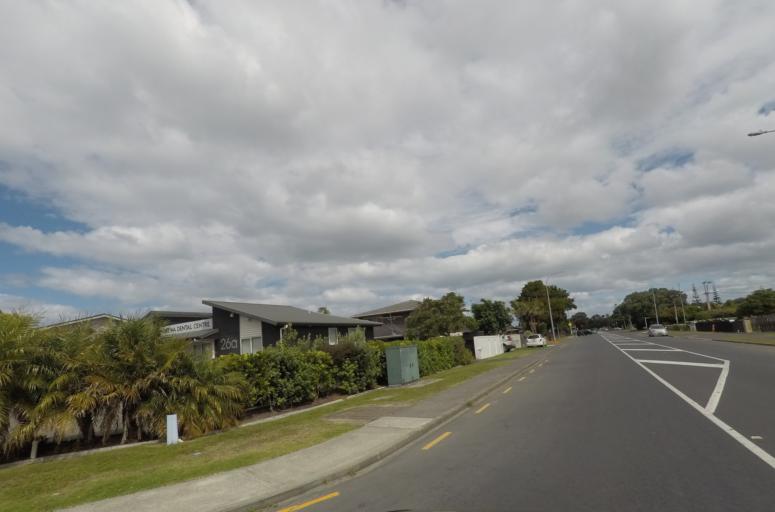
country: NZ
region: Auckland
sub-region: Auckland
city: Rothesay Bay
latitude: -36.5883
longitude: 174.6927
